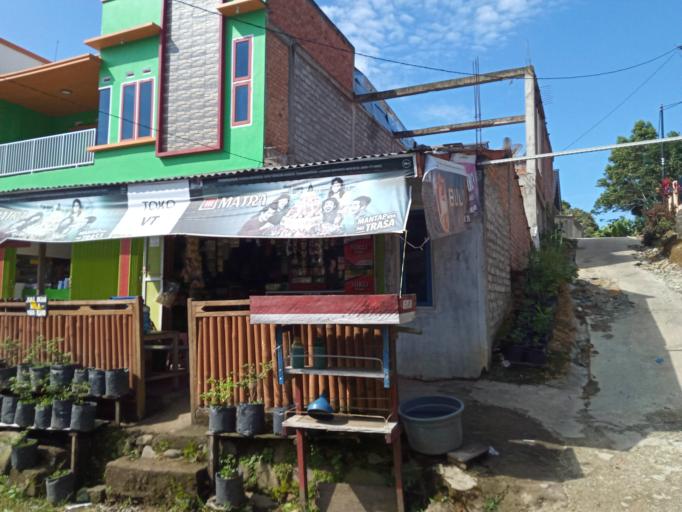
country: ID
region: Jambi
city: Sungai Penuh
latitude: -2.1629
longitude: 101.5896
